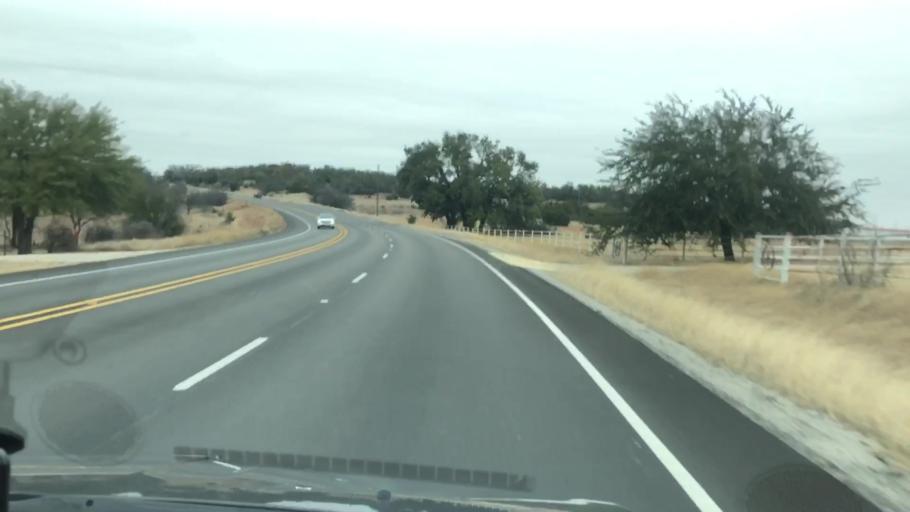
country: US
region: Texas
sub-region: Erath County
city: Stephenville
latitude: 32.4433
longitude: -98.1382
